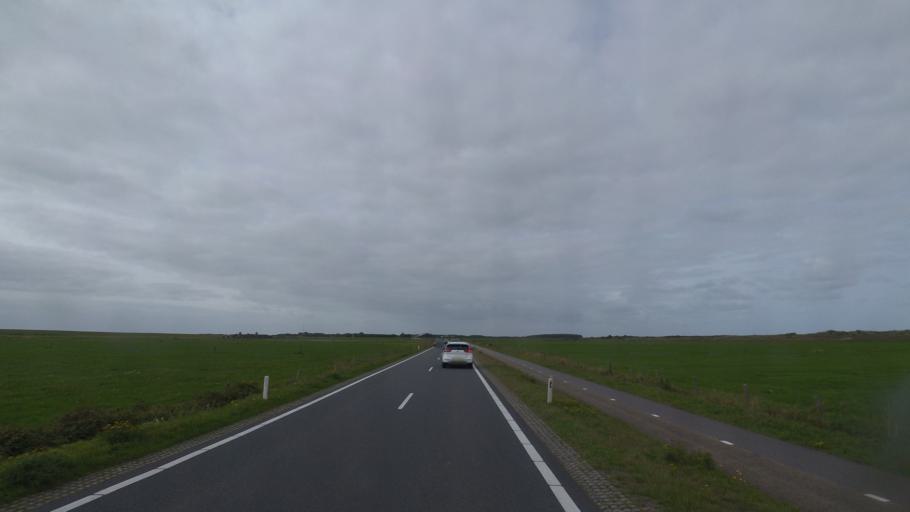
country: NL
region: Friesland
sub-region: Gemeente Ameland
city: Nes
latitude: 53.4460
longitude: 5.7427
